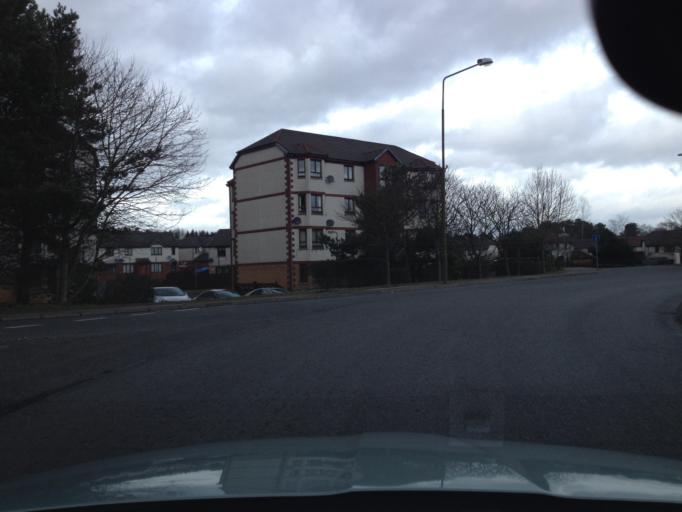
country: GB
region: Scotland
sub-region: West Lothian
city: Livingston
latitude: 55.9007
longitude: -3.5387
